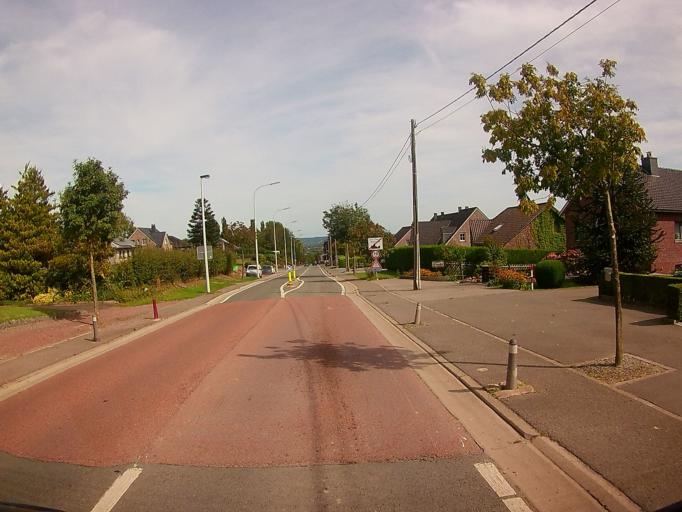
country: BE
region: Wallonia
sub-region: Province de Liege
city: Welkenraedt
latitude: 50.6784
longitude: 5.9344
